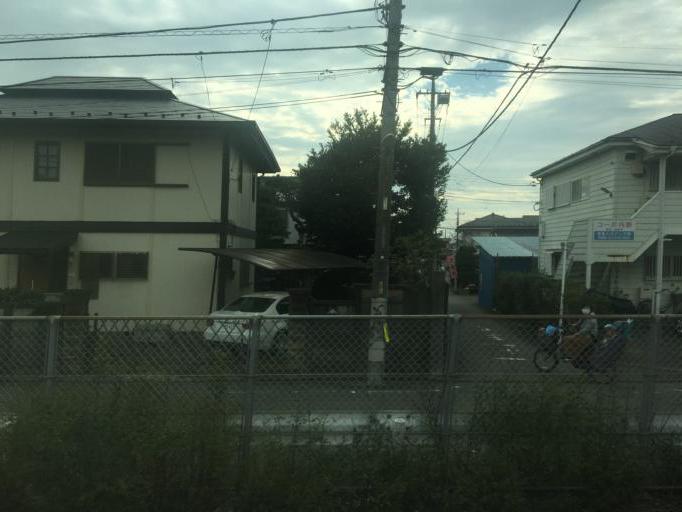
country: JP
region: Tokyo
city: Hino
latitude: 35.7102
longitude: 139.3718
